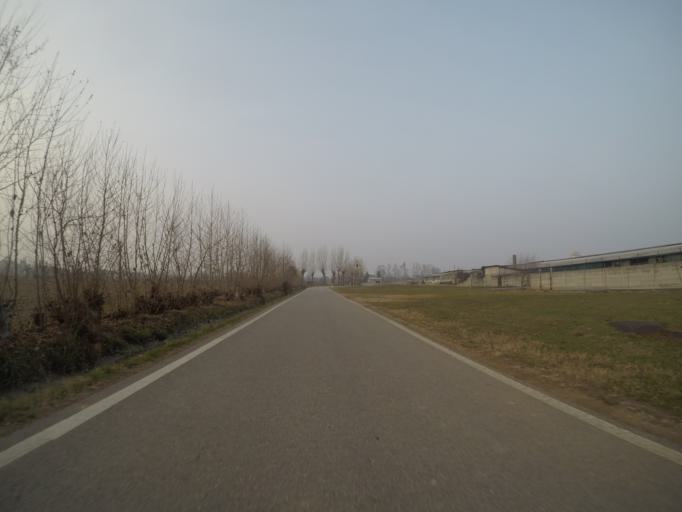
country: IT
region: Veneto
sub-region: Provincia di Treviso
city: Altivole
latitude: 45.7445
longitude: 11.9586
